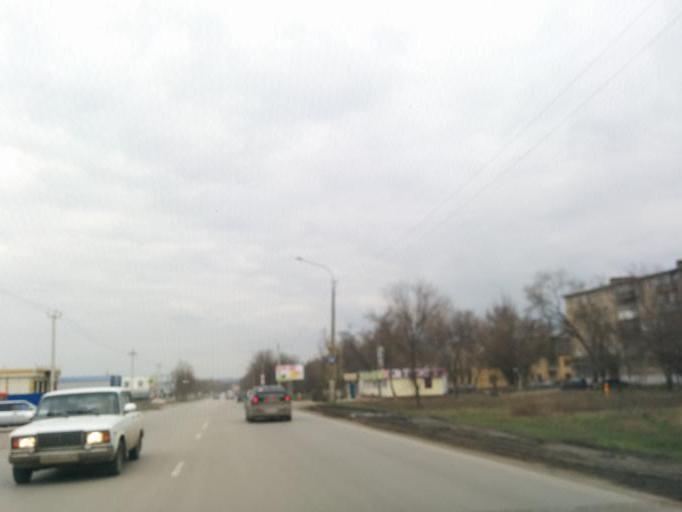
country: RU
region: Rostov
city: Krasyukovskaya
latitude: 47.4870
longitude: 40.1030
